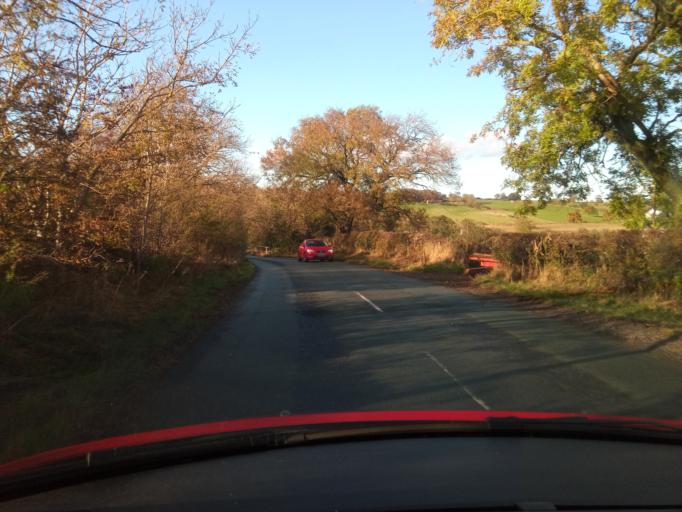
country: GB
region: England
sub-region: County Durham
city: Hamsterley
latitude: 54.6637
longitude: -1.8104
